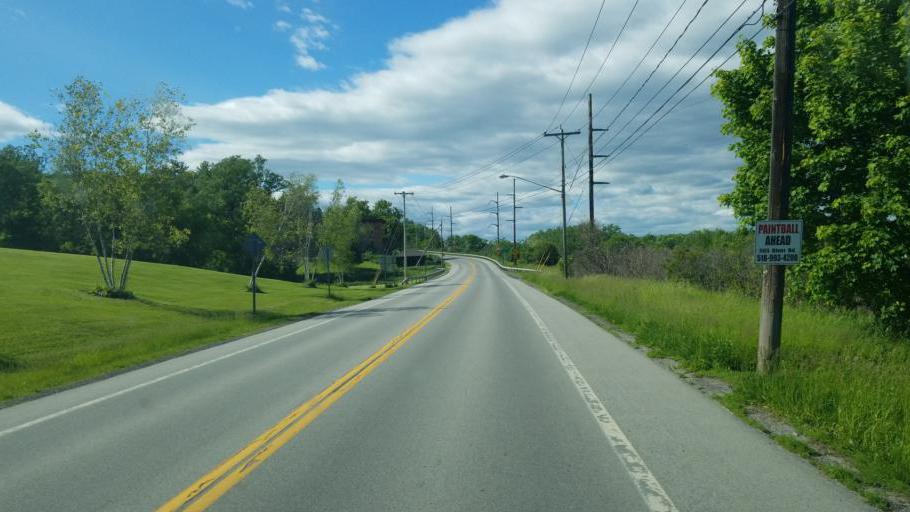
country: US
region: New York
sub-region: Montgomery County
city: Fort Plain
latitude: 42.9411
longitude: -74.6291
